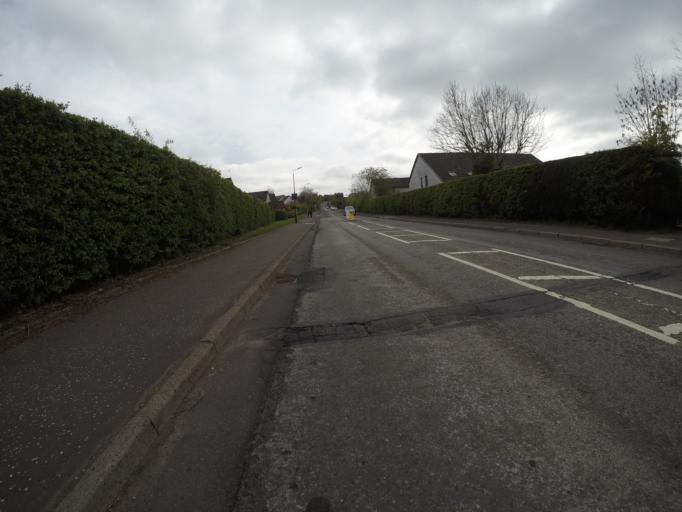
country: GB
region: Scotland
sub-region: East Renfrewshire
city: Busby
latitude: 55.7741
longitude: -4.3047
